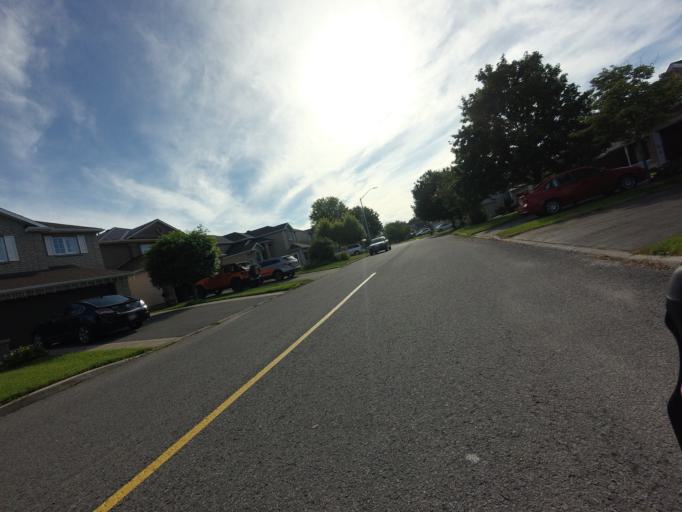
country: CA
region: Ontario
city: Ottawa
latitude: 45.2853
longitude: -75.6889
